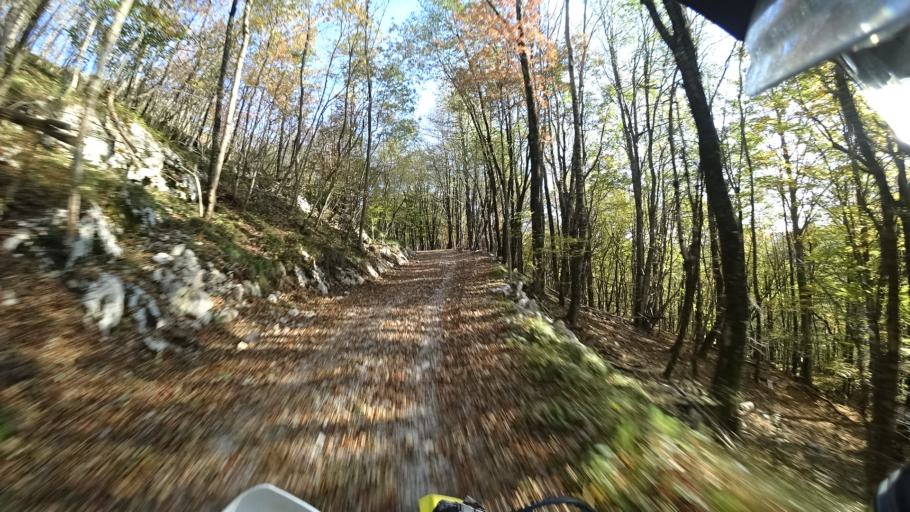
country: HR
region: Primorsko-Goranska
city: Klana
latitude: 45.4879
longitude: 14.4124
